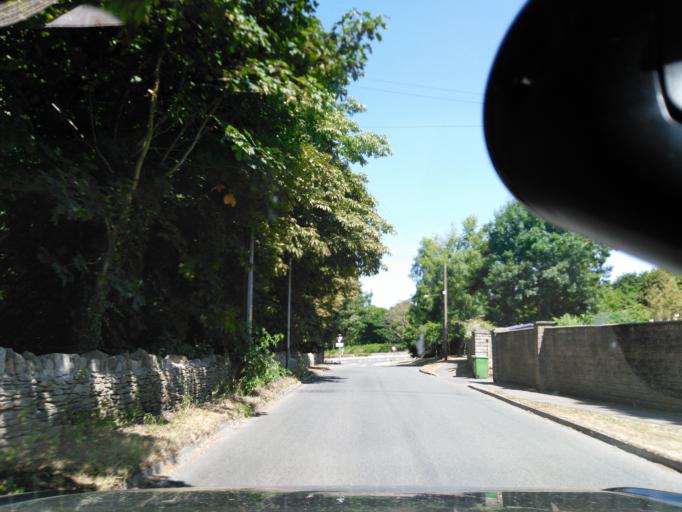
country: GB
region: England
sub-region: Wiltshire
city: Box
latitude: 51.4299
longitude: -2.2262
